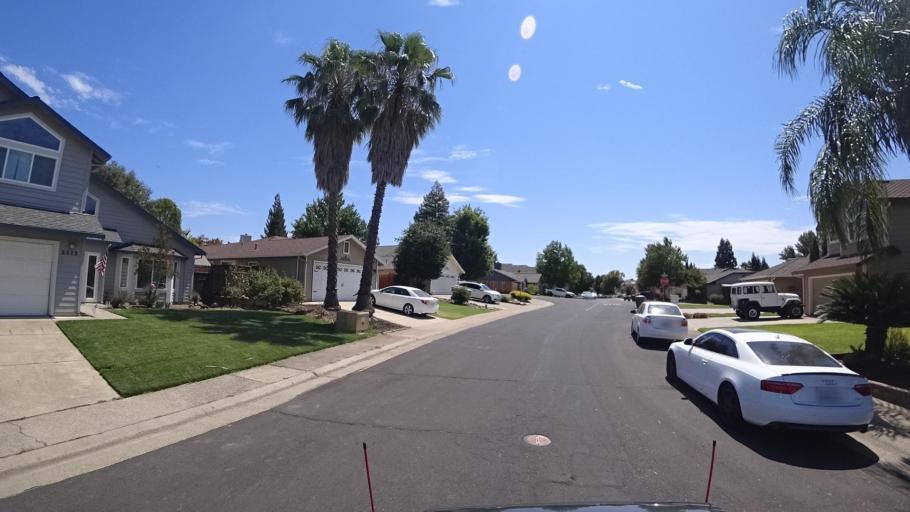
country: US
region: California
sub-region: Placer County
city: Rocklin
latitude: 38.8064
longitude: -121.2616
